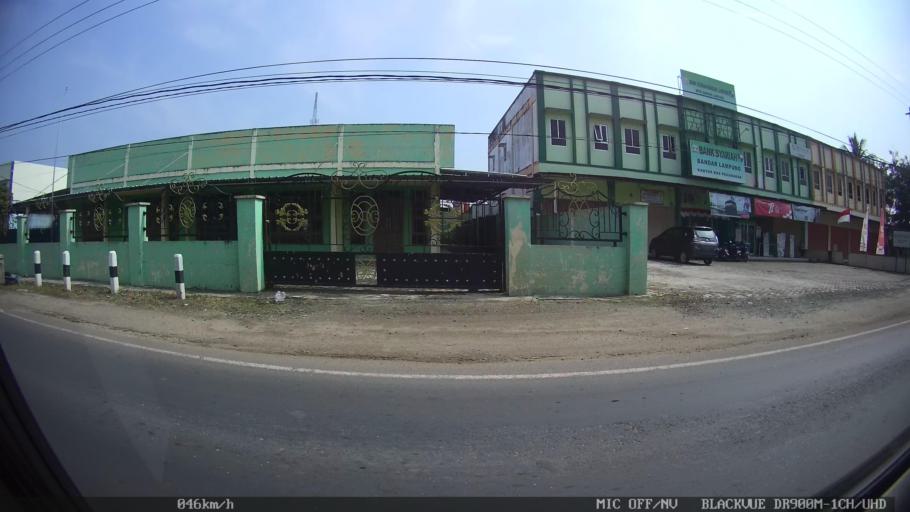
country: ID
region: Lampung
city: Gedongtataan
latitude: -5.3753
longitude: 105.0866
